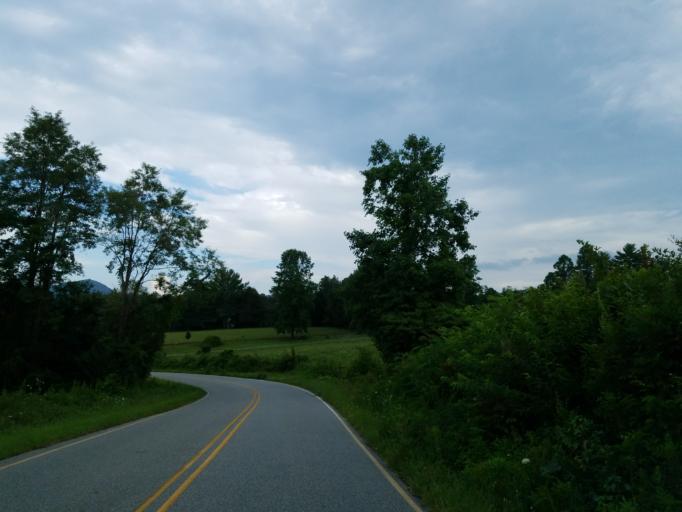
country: US
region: Georgia
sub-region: Fannin County
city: Blue Ridge
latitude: 34.8459
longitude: -84.2294
